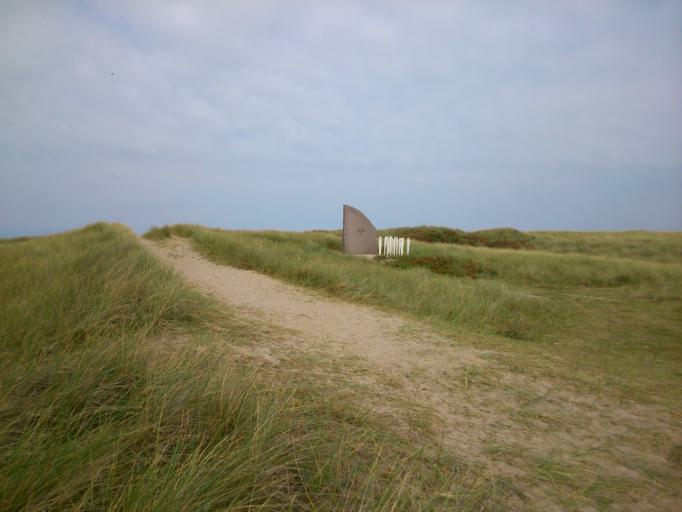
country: DK
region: Central Jutland
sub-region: Lemvig Kommune
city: Thyboron
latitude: 56.7068
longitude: 8.2125
